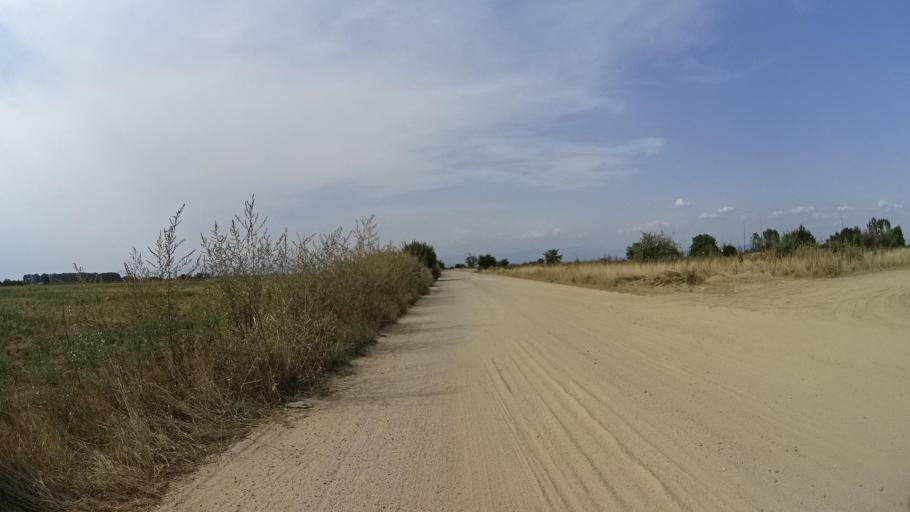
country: BG
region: Plovdiv
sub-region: Obshtina Kaloyanovo
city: Kaloyanovo
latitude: 42.3133
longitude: 24.7995
